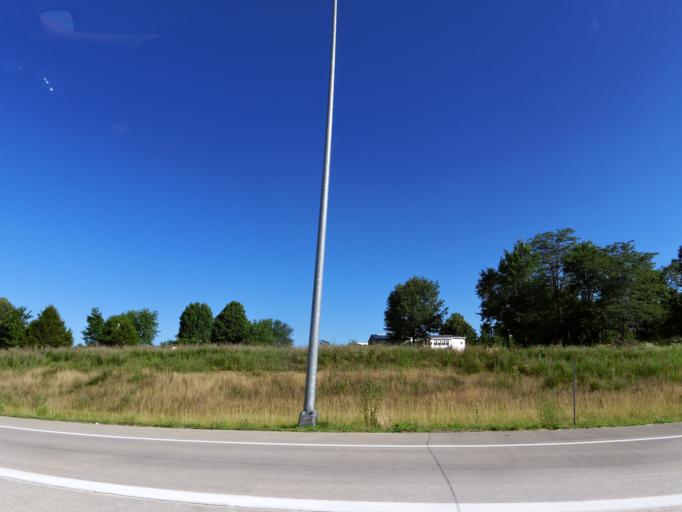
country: US
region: Missouri
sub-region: Butler County
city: Poplar Bluff
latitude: 36.6664
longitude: -90.5125
